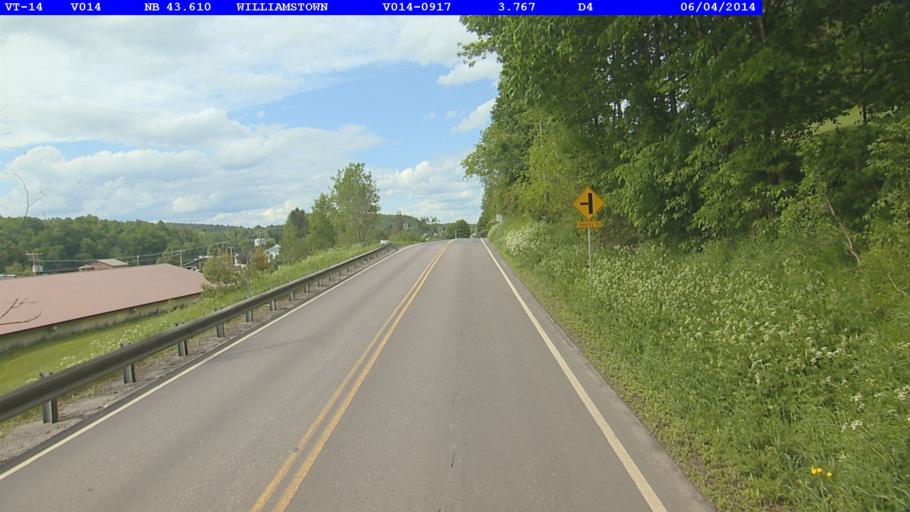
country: US
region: Vermont
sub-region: Orange County
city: Williamstown
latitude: 44.1122
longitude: -72.5399
